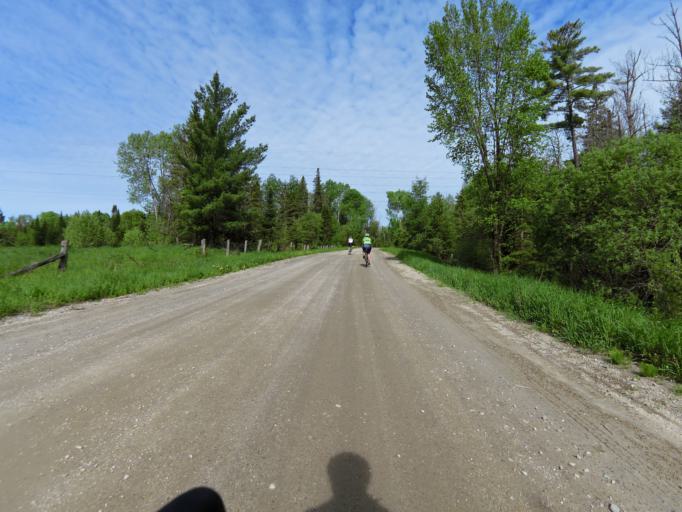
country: CA
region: Quebec
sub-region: Outaouais
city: Wakefield
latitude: 45.6954
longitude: -75.8908
